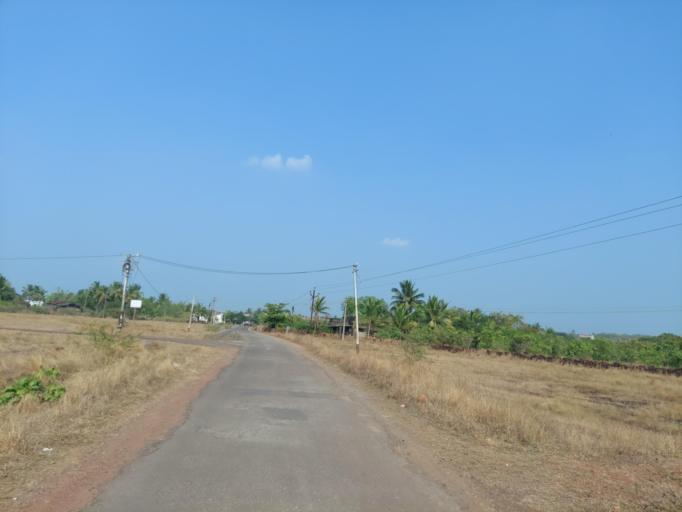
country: IN
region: Maharashtra
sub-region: Ratnagiri
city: Ratnagiri
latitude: 16.9307
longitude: 73.3231
